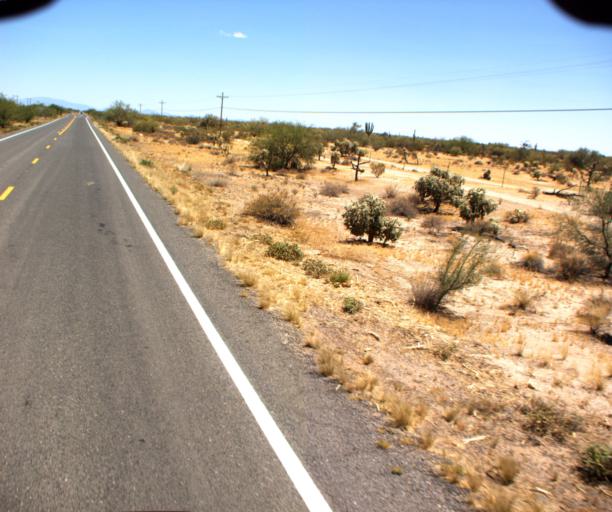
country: US
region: Arizona
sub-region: Pinal County
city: Florence
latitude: 32.9184
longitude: -111.2955
